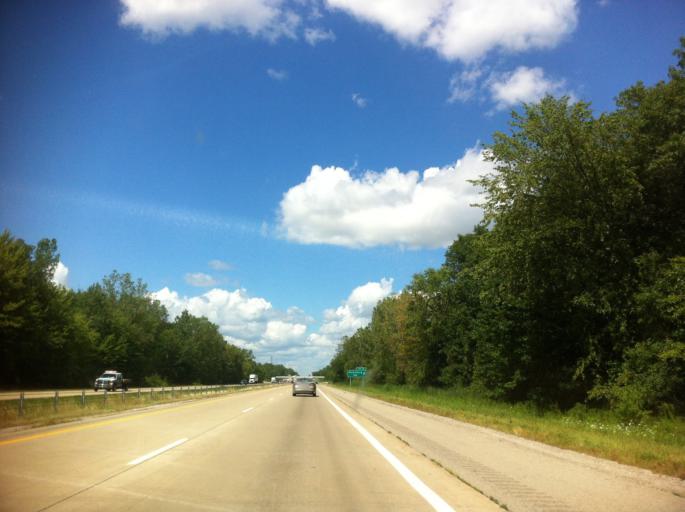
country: US
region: Michigan
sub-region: Monroe County
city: Petersburg
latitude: 41.9024
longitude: -83.6616
